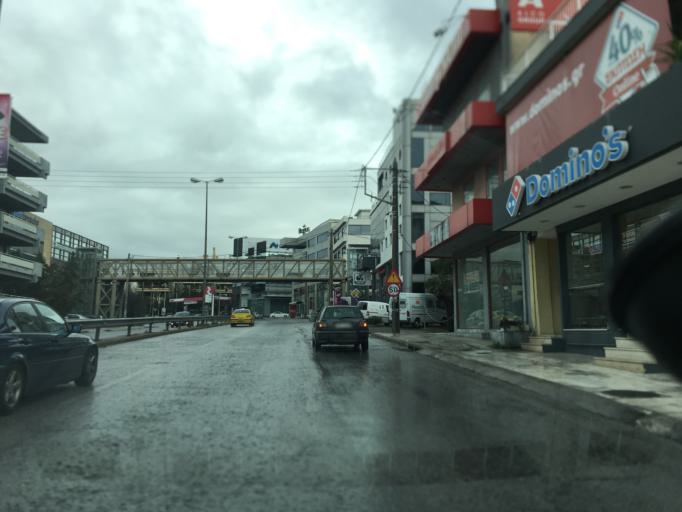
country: GR
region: Attica
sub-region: Nomarchia Athinas
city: Marousi
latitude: 38.0547
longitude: 23.8117
